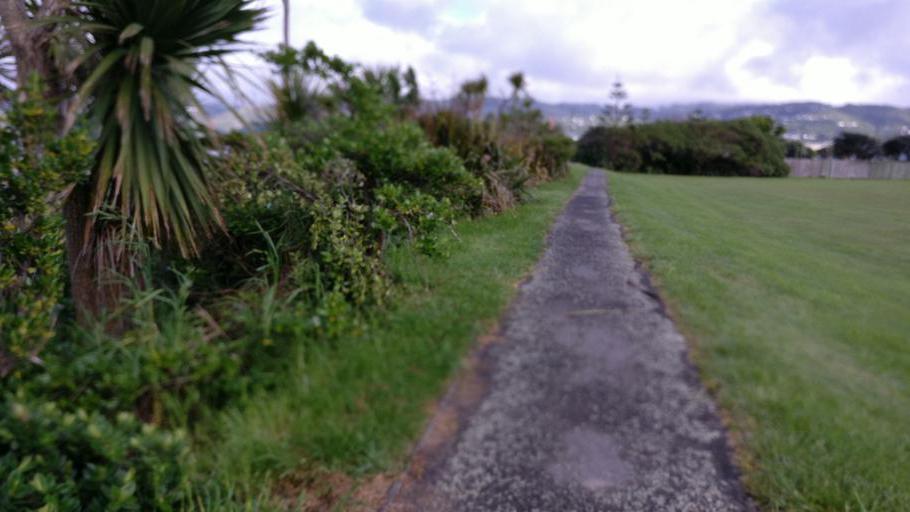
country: NZ
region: Wellington
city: Petone
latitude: -41.2339
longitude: 174.8926
